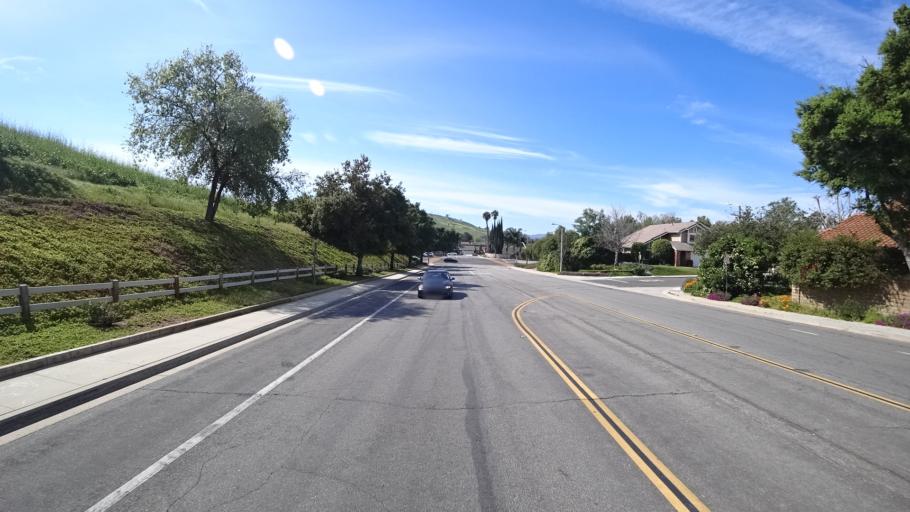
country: US
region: California
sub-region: Ventura County
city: Thousand Oaks
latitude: 34.2128
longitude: -118.8357
